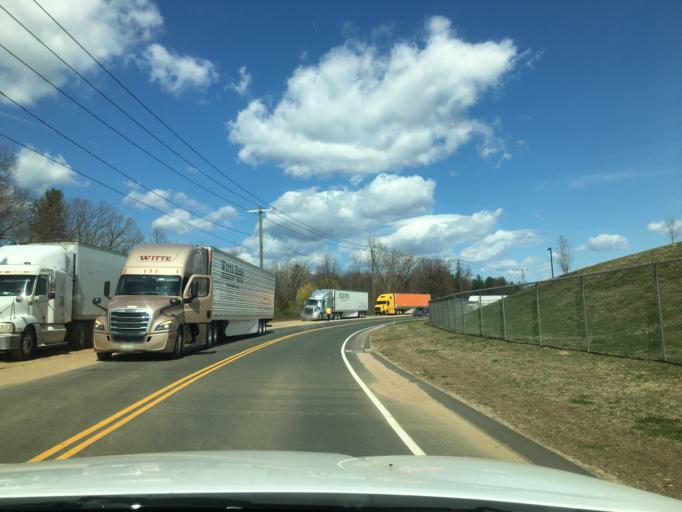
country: US
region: Connecticut
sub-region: Hartford County
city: Blue Hills
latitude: 41.8688
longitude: -72.7109
